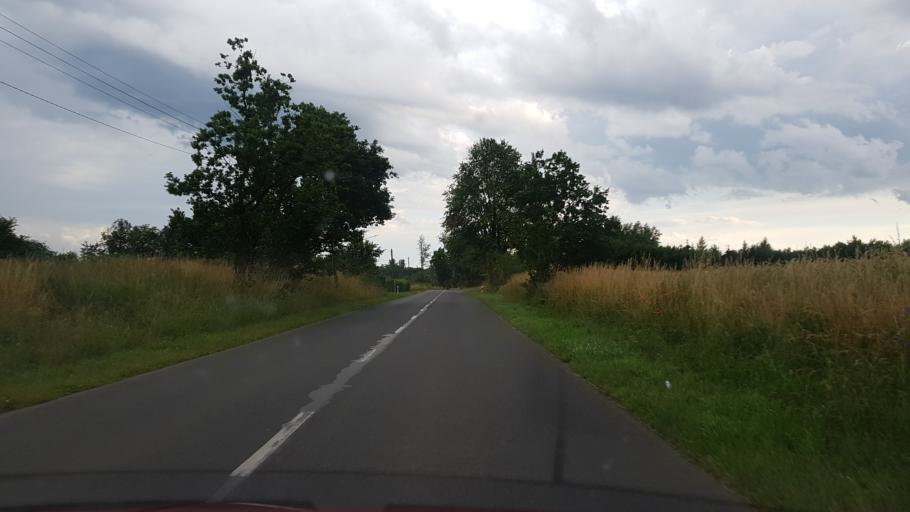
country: PL
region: West Pomeranian Voivodeship
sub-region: Powiat gryficki
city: Gryfice
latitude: 53.8458
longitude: 15.1005
